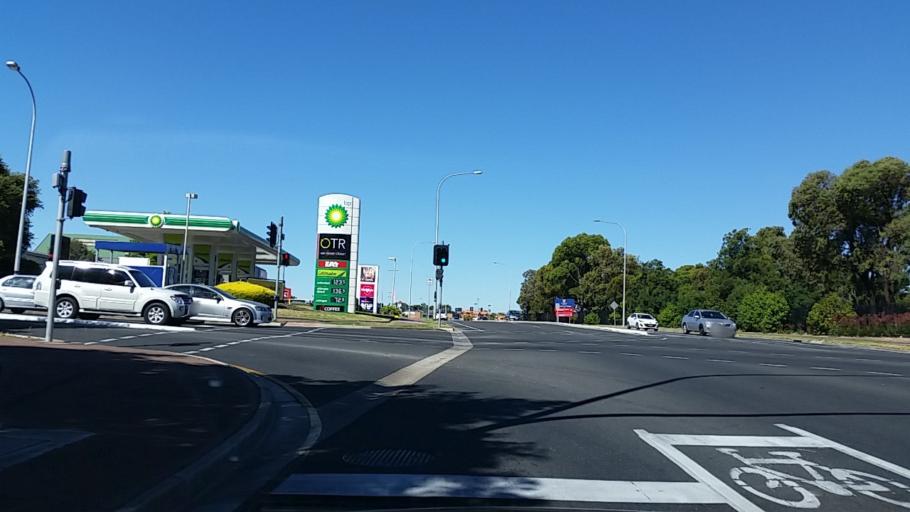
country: AU
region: South Australia
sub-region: Tea Tree Gully
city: Hope Valley
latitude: -34.7937
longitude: 138.6917
